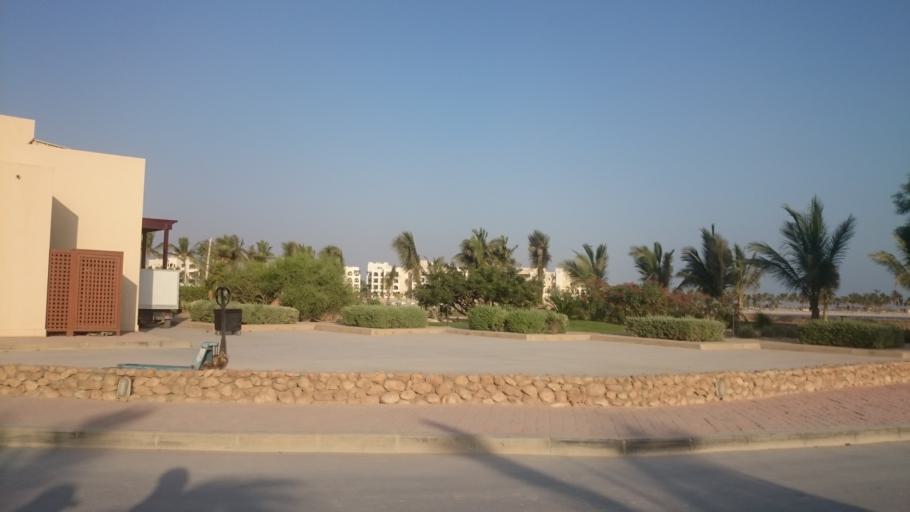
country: OM
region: Zufar
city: Salalah
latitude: 17.0306
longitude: 54.2987
